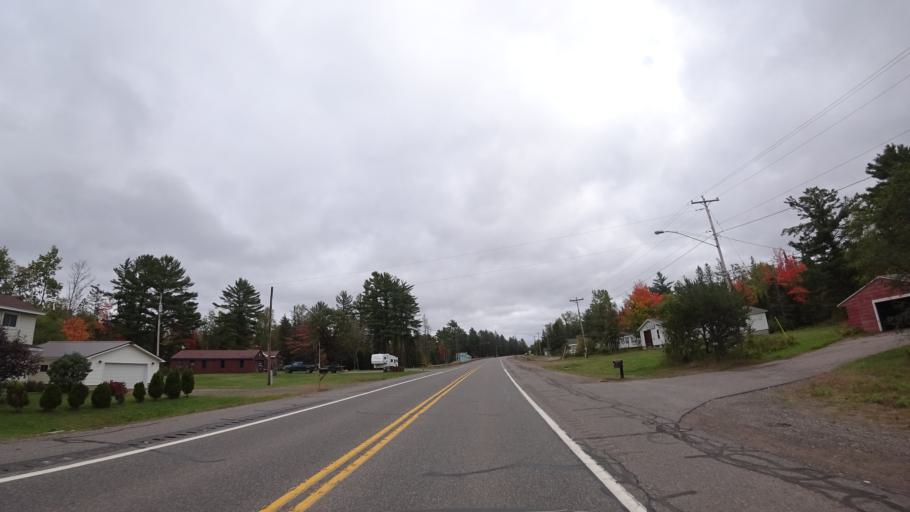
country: US
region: Michigan
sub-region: Marquette County
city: West Ishpeming
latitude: 46.4993
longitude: -87.9439
